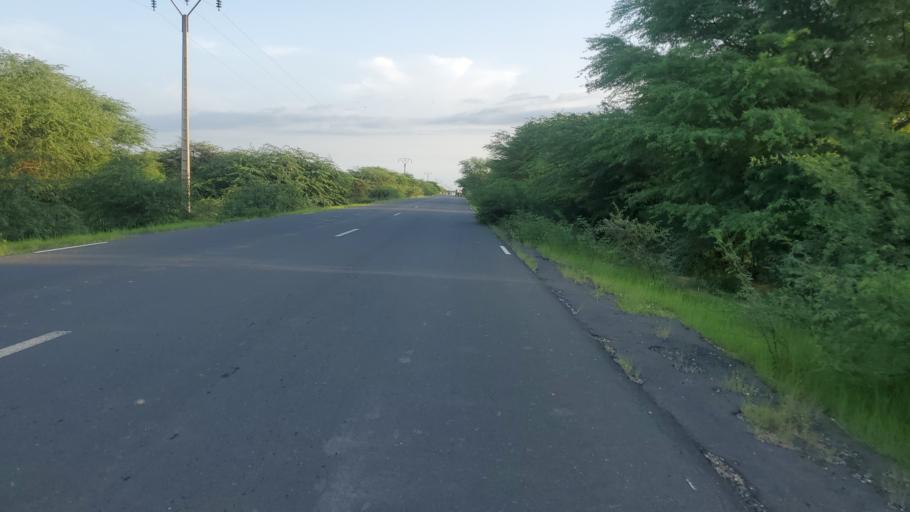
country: SN
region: Saint-Louis
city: Saint-Louis
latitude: 16.1911
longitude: -16.4092
